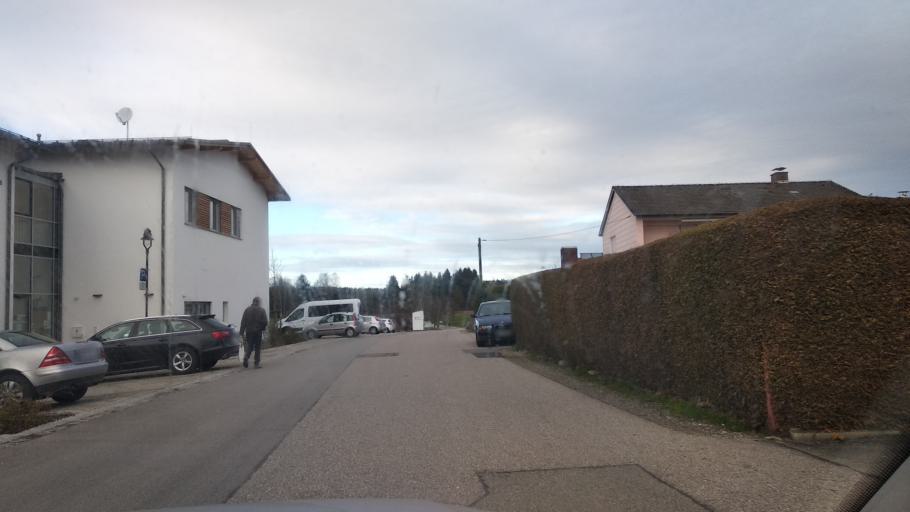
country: DE
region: Bavaria
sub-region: Upper Bavaria
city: Ebersberg
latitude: 48.0761
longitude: 11.9524
